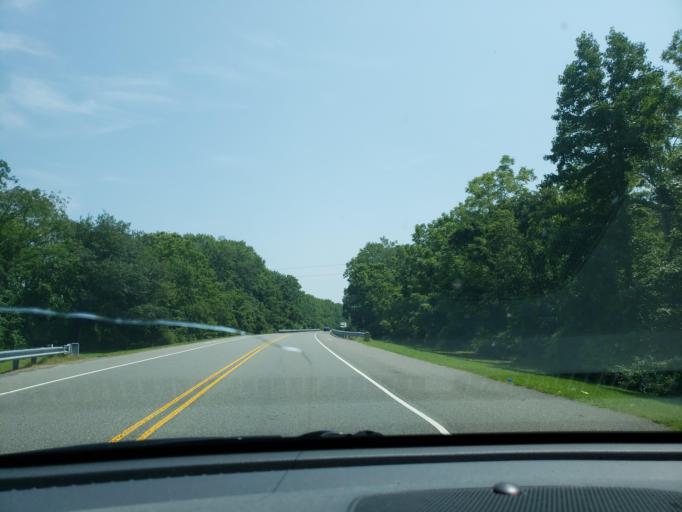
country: US
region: New Jersey
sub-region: Cape May County
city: Erma
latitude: 38.9735
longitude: -74.9330
